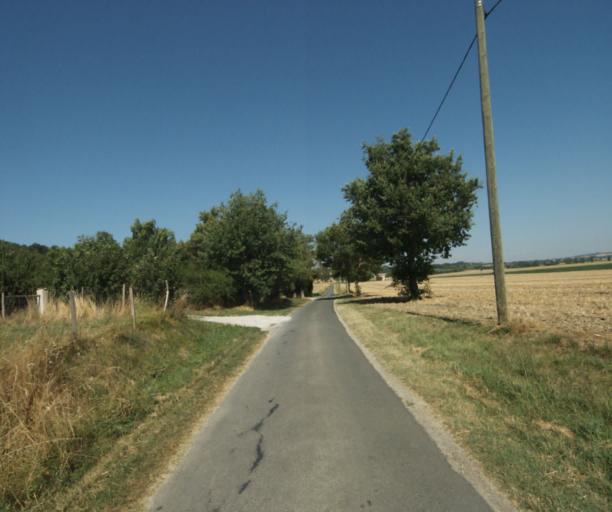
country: FR
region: Midi-Pyrenees
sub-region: Departement de la Haute-Garonne
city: Revel
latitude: 43.5170
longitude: 1.9476
